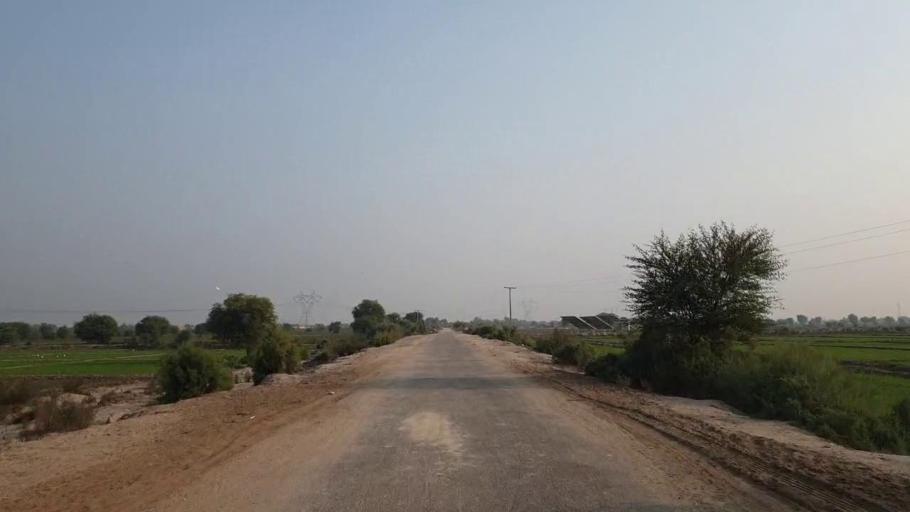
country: PK
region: Sindh
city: Bhan
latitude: 26.4966
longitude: 67.7680
